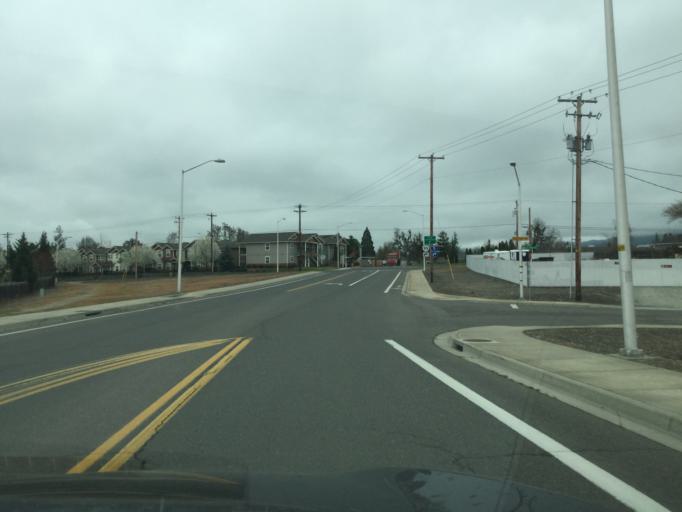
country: US
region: Oregon
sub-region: Jackson County
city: Central Point
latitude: 42.3887
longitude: -122.9204
